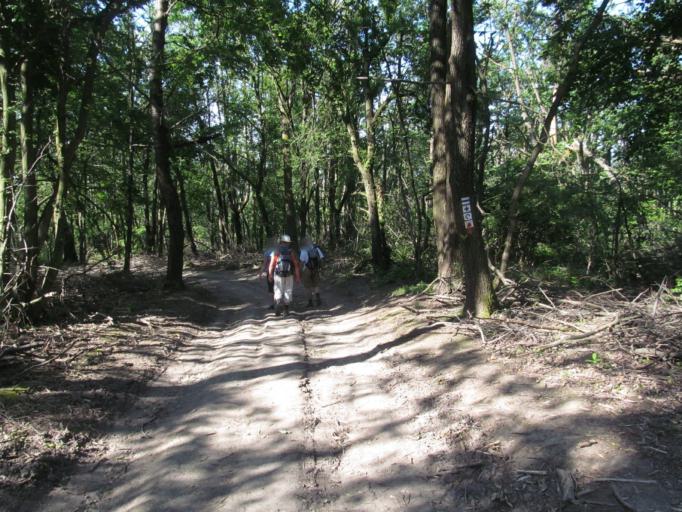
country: HU
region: Pest
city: Pilisszentkereszt
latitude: 47.7173
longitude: 18.9054
